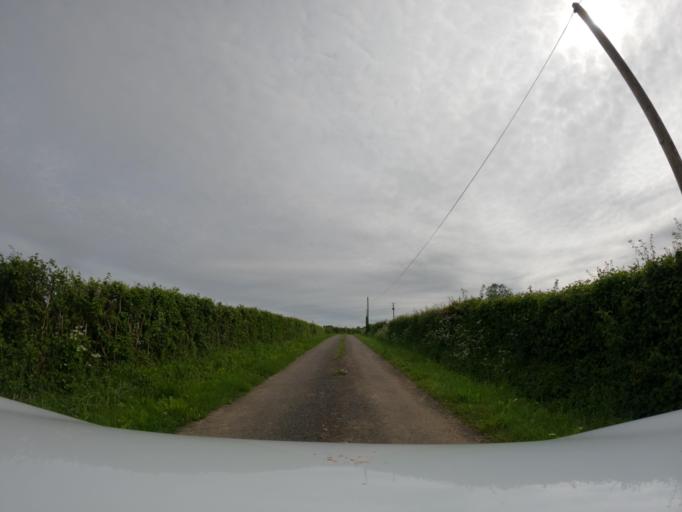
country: FR
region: Pays de la Loire
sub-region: Departement de la Vendee
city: Saint-Hilaire-des-Loges
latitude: 46.4971
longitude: -0.6687
